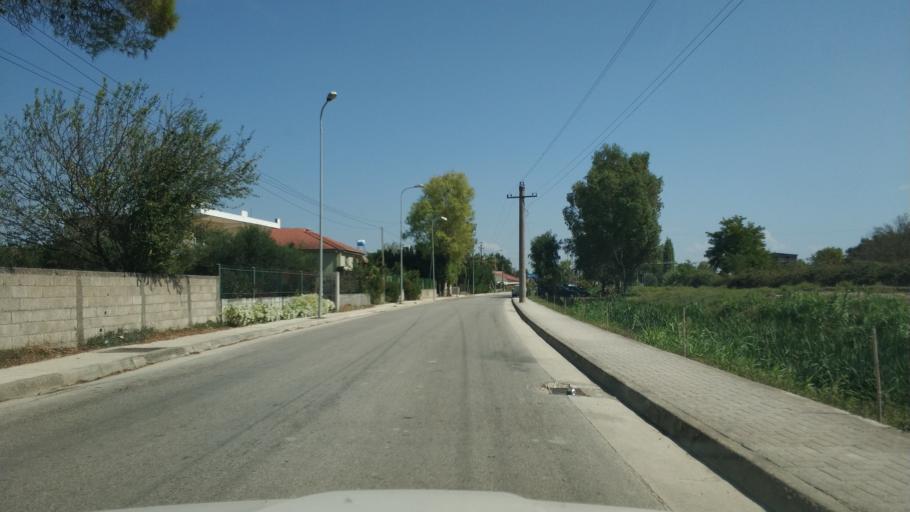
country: AL
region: Fier
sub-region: Rrethi i Lushnjes
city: Gradishte
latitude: 40.8930
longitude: 19.6189
